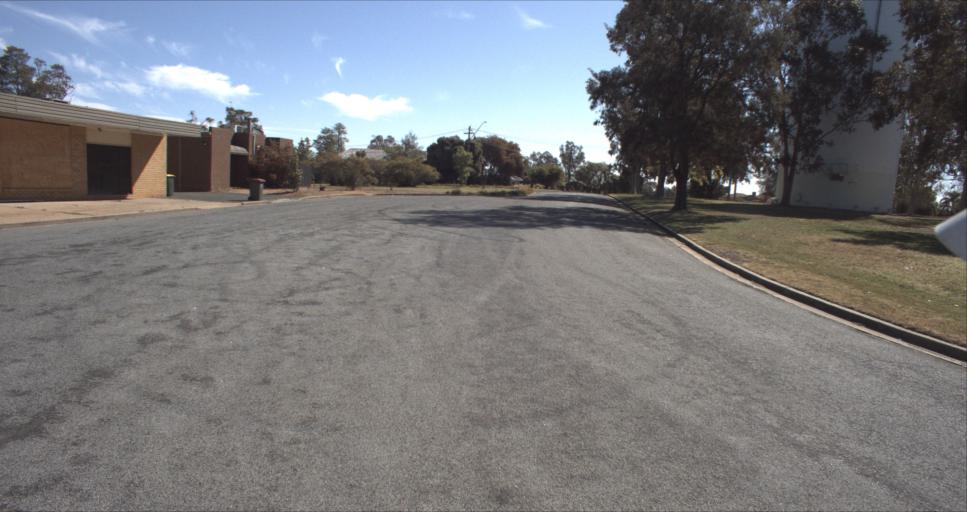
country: AU
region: New South Wales
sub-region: Leeton
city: Leeton
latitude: -34.5505
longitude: 146.3773
